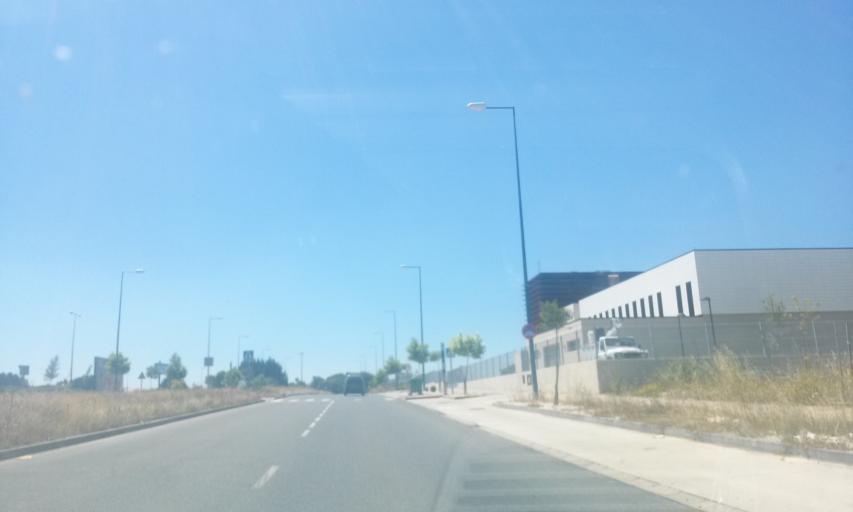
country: ES
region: Galicia
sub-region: Provincia de Lugo
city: Lugo
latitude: 43.0371
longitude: -7.5548
